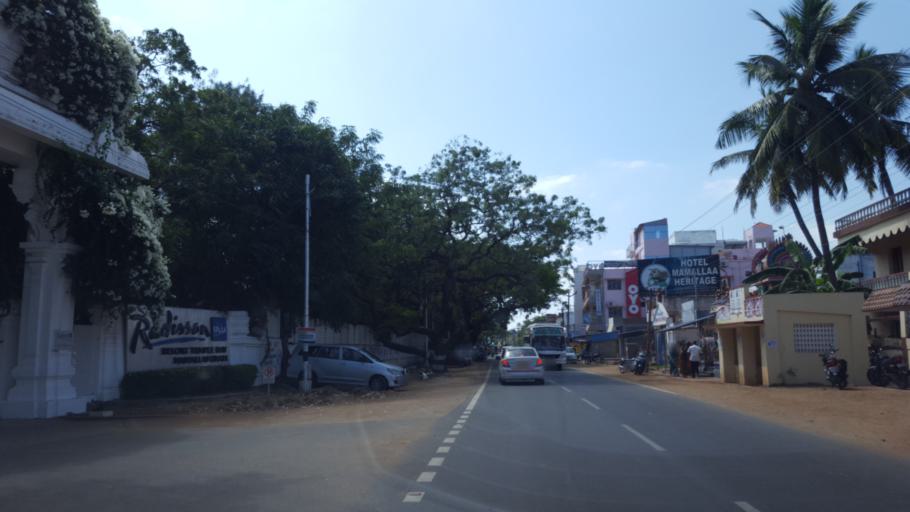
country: IN
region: Tamil Nadu
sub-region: Kancheepuram
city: Mamallapuram
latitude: 12.6249
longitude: 80.1943
